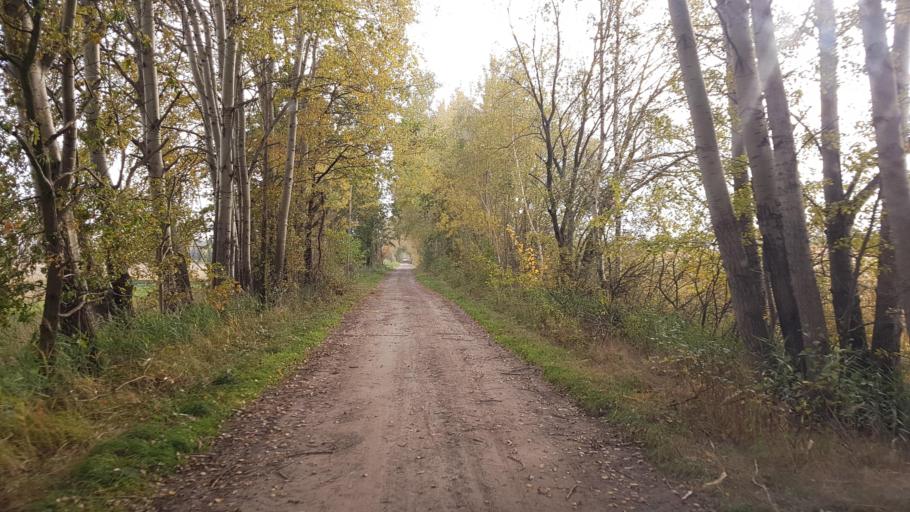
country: DE
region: Brandenburg
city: Schraden
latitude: 51.4506
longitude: 13.6918
